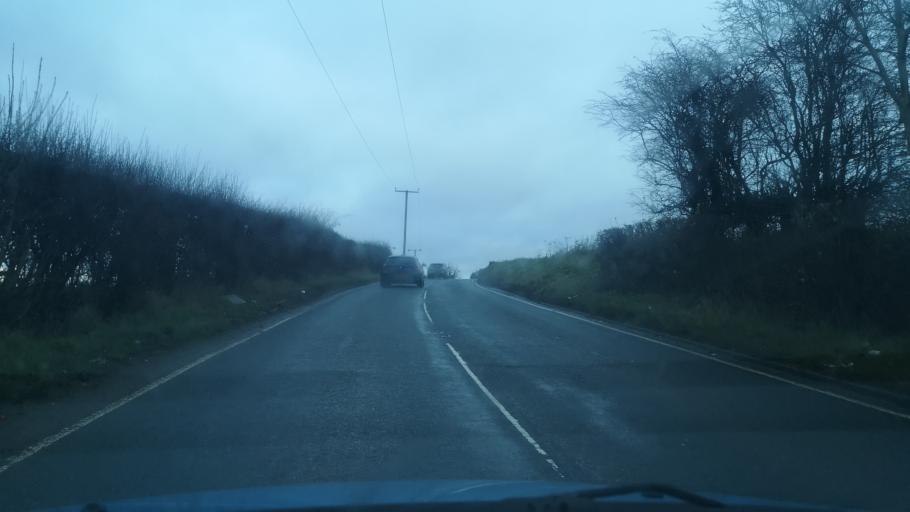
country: GB
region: England
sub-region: City and Borough of Wakefield
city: Fitzwilliam
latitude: 53.6444
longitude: -1.3727
